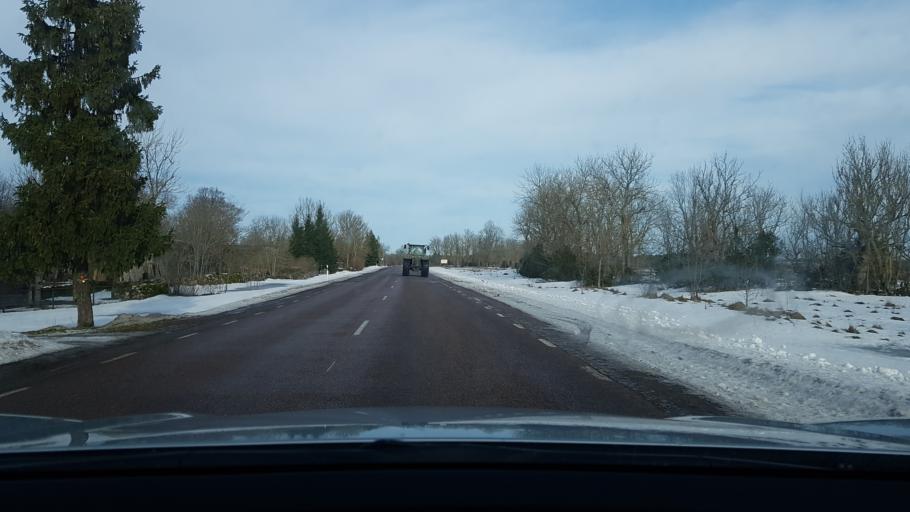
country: EE
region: Saare
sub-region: Kuressaare linn
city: Kuressaare
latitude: 58.3268
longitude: 22.5563
